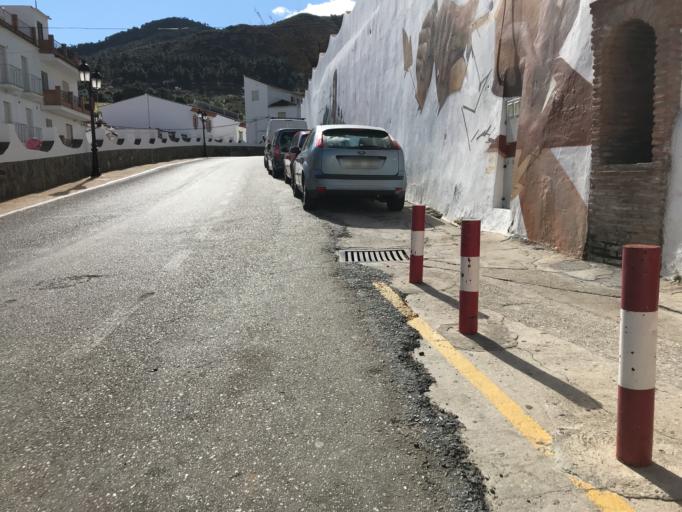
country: ES
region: Andalusia
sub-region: Provincia de Malaga
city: Tolox
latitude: 36.6849
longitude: -4.9048
